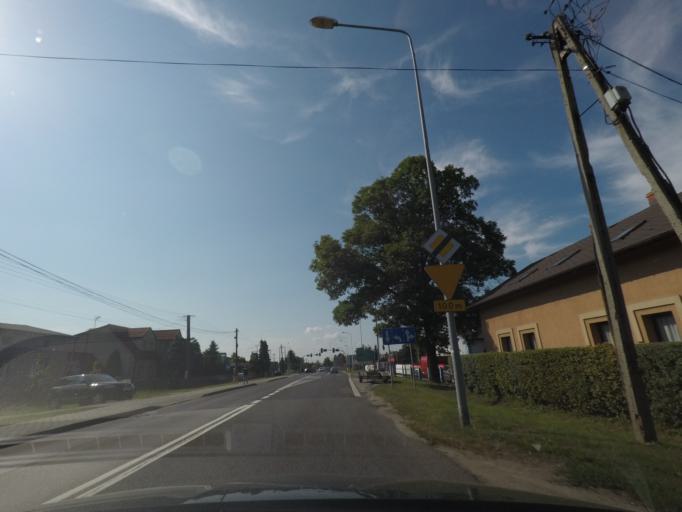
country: PL
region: Silesian Voivodeship
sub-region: Zory
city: Zory
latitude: 50.0540
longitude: 18.6815
